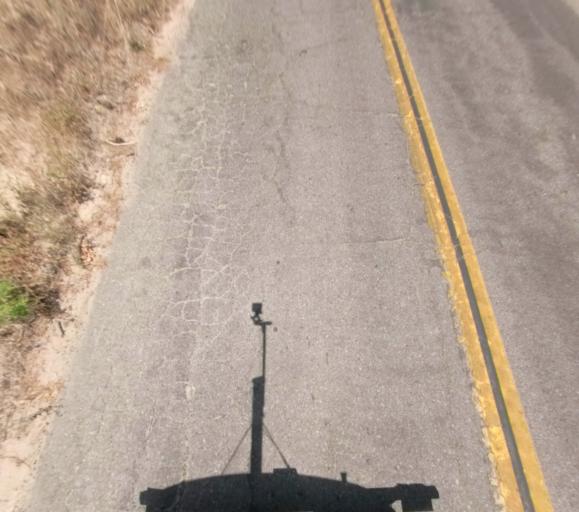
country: US
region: California
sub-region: Madera County
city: Oakhurst
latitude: 37.3113
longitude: -119.5537
